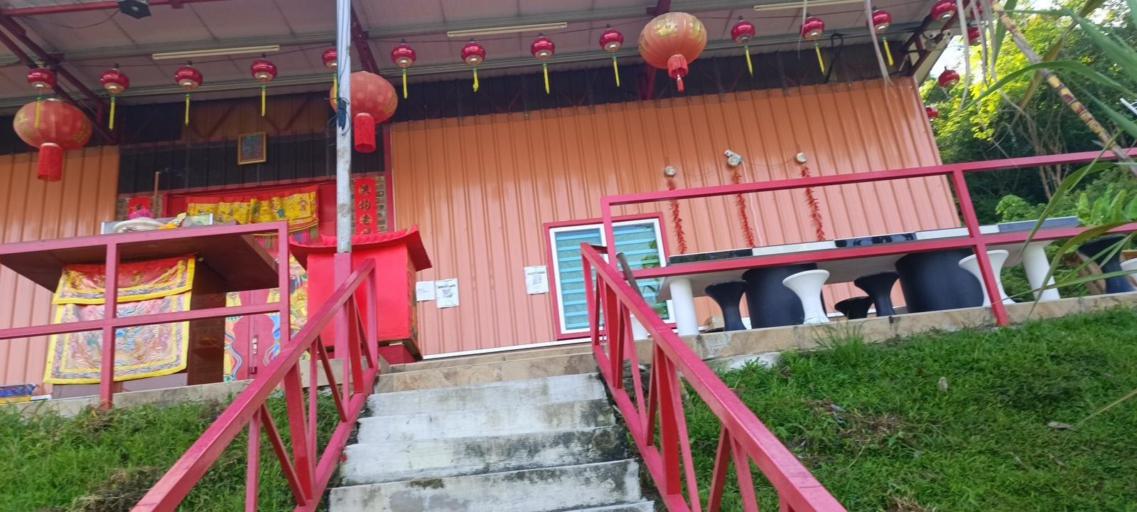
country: MY
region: Penang
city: Nibong Tebal
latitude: 5.2322
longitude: 100.5124
